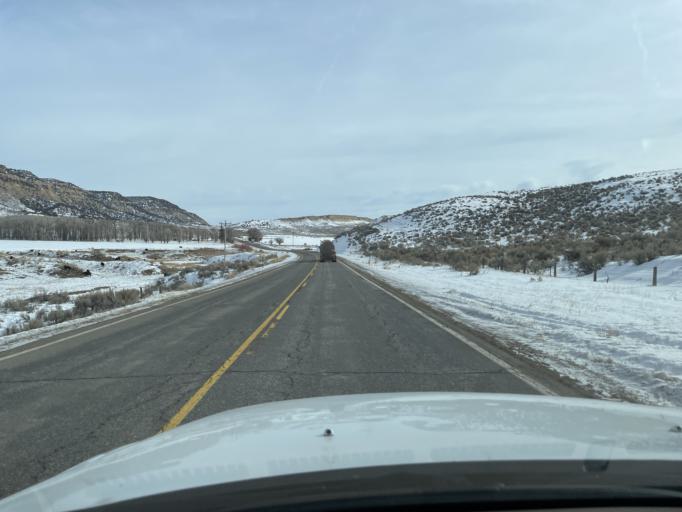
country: US
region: Colorado
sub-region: Moffat County
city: Craig
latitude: 40.3345
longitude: -107.6930
